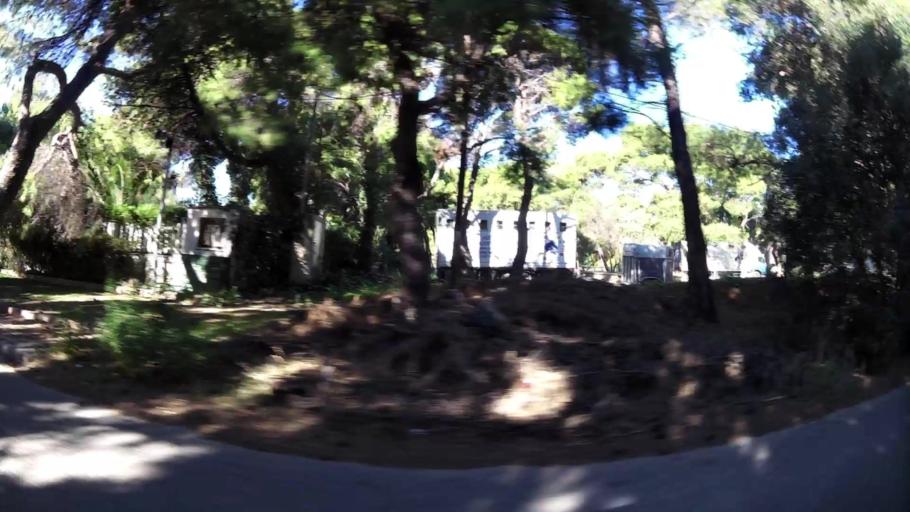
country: GR
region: Attica
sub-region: Nomarchia Anatolikis Attikis
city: Varybobi
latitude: 38.1252
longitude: 23.7938
